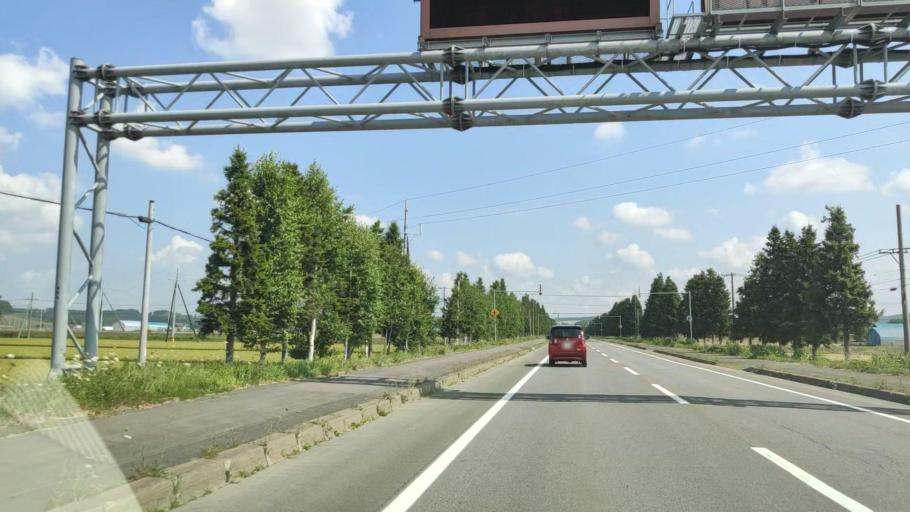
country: JP
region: Hokkaido
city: Shimo-furano
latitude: 43.4788
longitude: 142.4589
